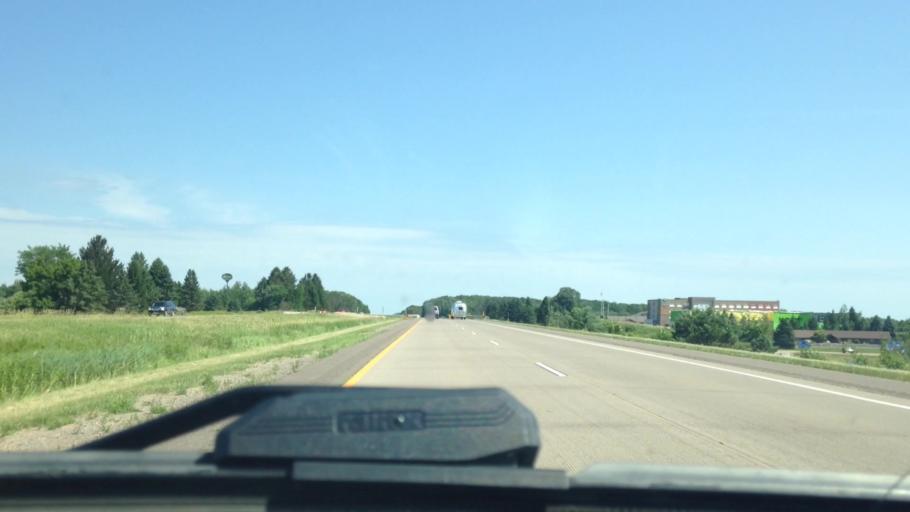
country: US
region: Wisconsin
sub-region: Barron County
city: Rice Lake
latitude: 45.5067
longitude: -91.7623
